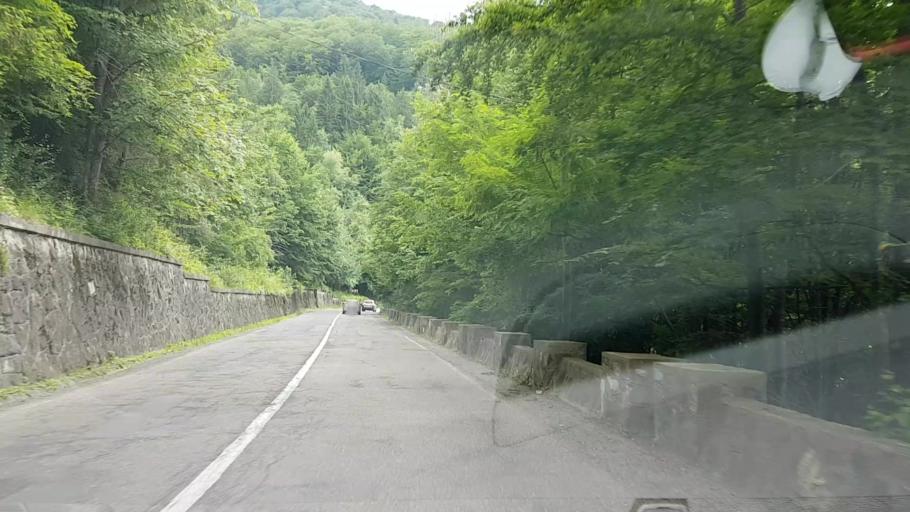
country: RO
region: Neamt
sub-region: Comuna Bicaz
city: Dodeni
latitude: 46.9392
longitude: 26.1145
